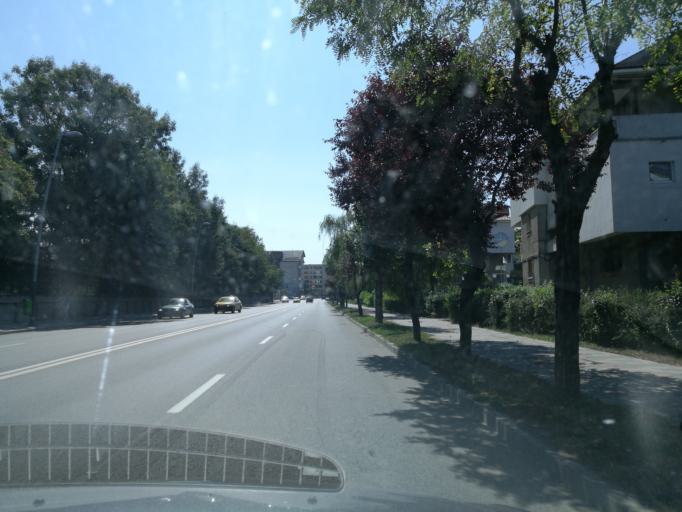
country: RO
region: Bacau
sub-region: Municipiul Bacau
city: Bacau
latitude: 46.5666
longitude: 26.9223
